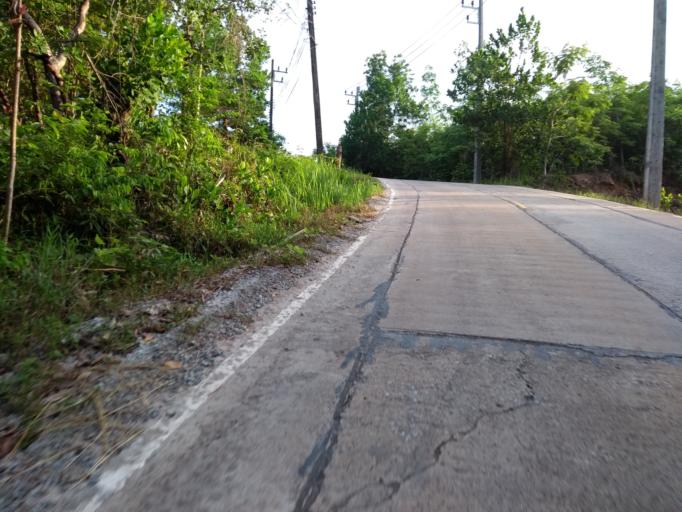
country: TH
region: Trat
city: Ko Kut
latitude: 11.6256
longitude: 102.5468
